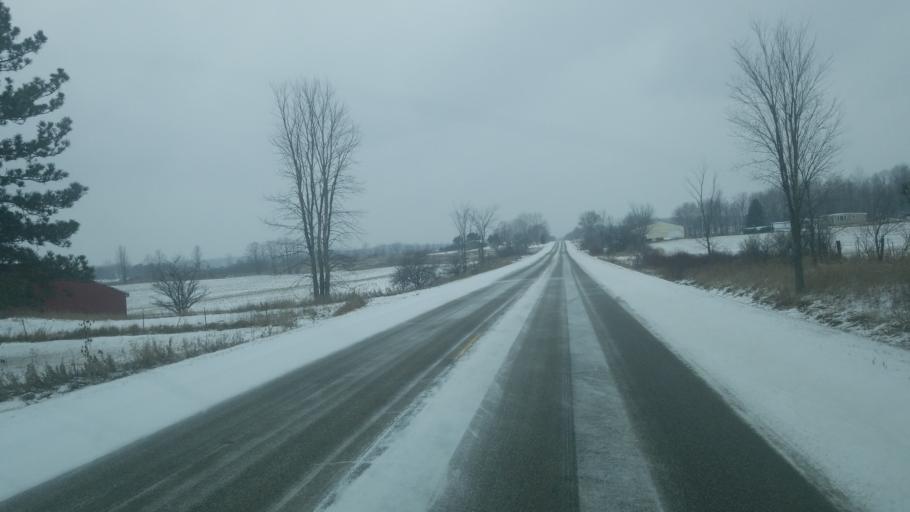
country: US
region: Michigan
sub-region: Osceola County
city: Evart
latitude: 44.1025
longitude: -85.1789
